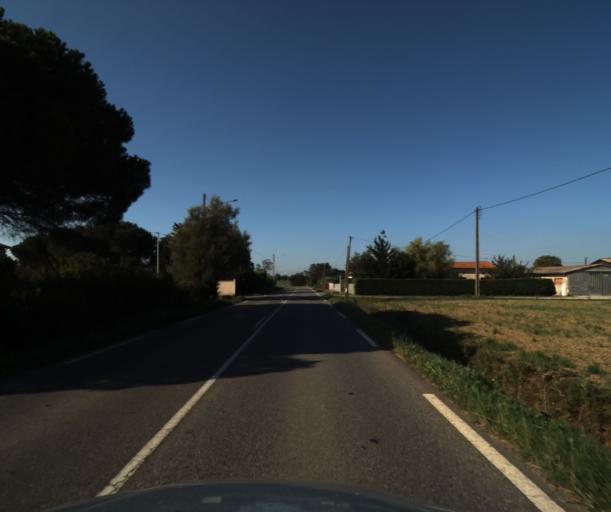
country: FR
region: Midi-Pyrenees
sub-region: Departement de la Haute-Garonne
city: Lagardelle-sur-Leze
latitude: 43.4296
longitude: 1.3781
